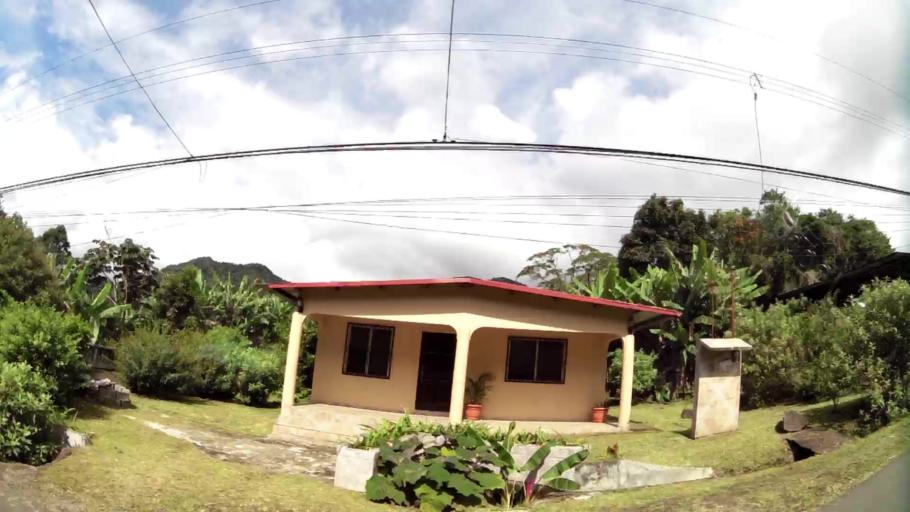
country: PA
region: Chiriqui
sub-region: Distrito Boquete
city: Boquete
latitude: 8.8012
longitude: -82.4256
